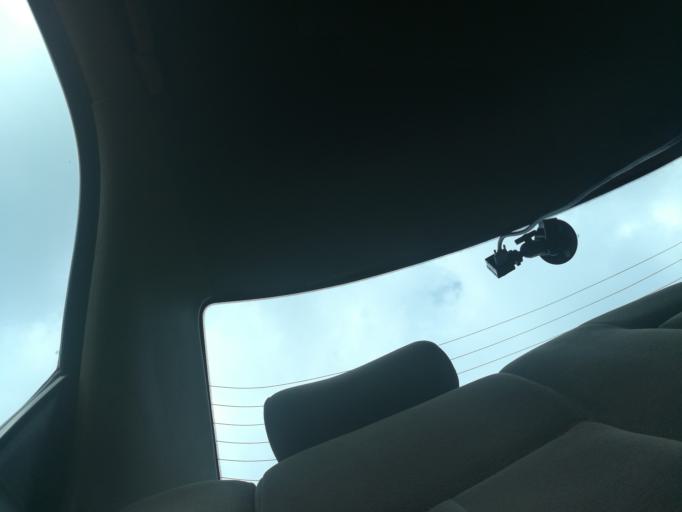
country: NG
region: Lagos
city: Ikorodu
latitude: 6.6545
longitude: 3.5804
